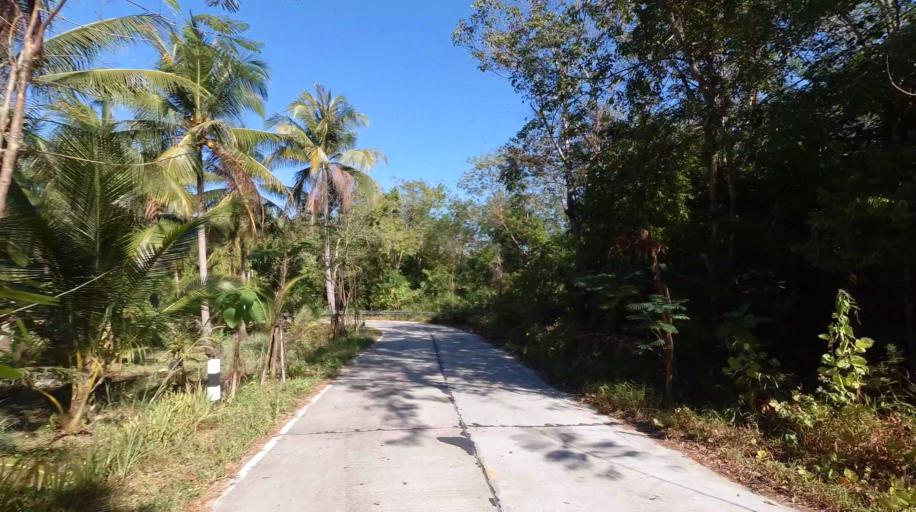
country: TH
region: Trat
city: Ko Kut
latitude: 11.6151
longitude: 102.5422
